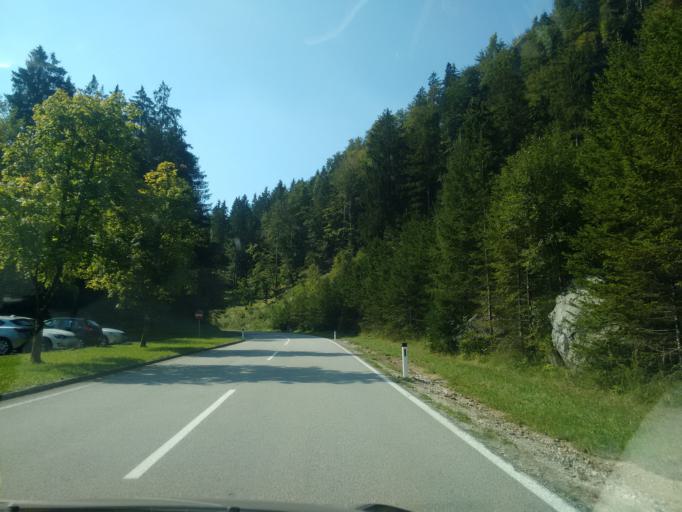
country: AT
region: Upper Austria
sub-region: Politischer Bezirk Gmunden
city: Gruenau im Almtal
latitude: 47.7777
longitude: 13.9605
